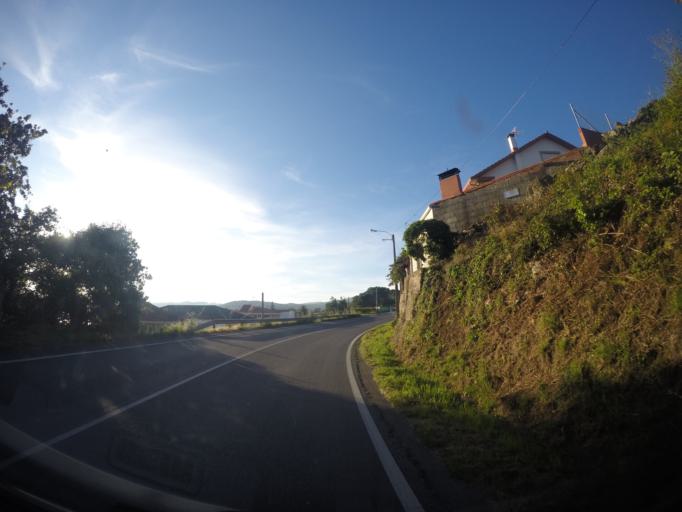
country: ES
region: Galicia
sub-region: Provincia da Coruna
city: Noia
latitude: 42.7666
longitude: -8.9378
